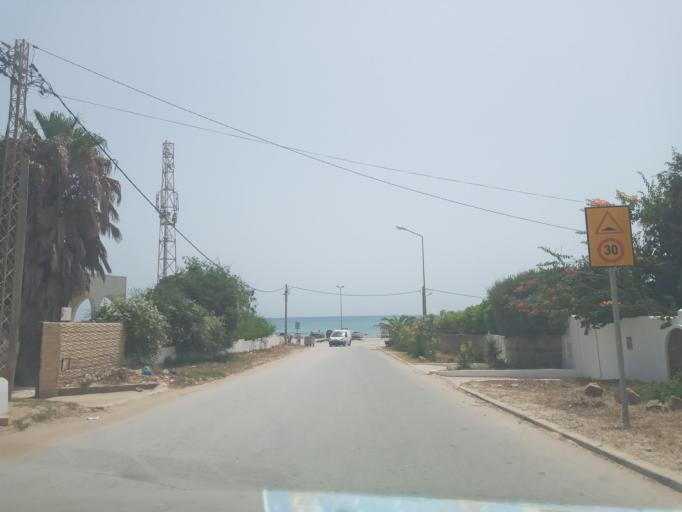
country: TN
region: Nabul
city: El Haouaria
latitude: 37.0359
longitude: 11.0575
